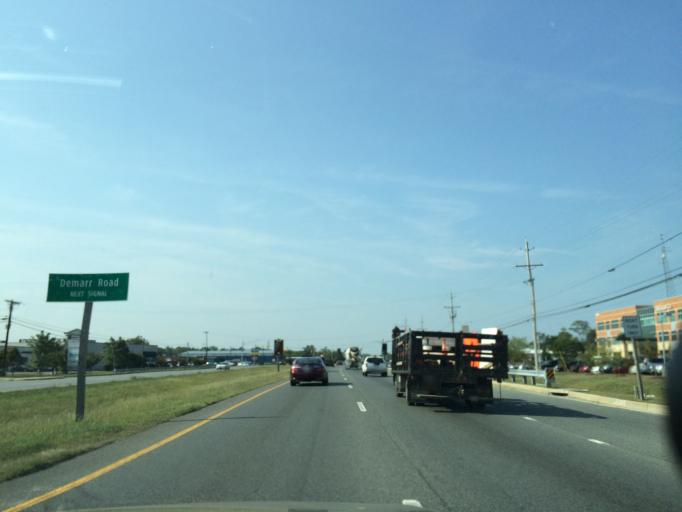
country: US
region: Maryland
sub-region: Charles County
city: Saint Charles
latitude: 38.5932
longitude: -76.9399
